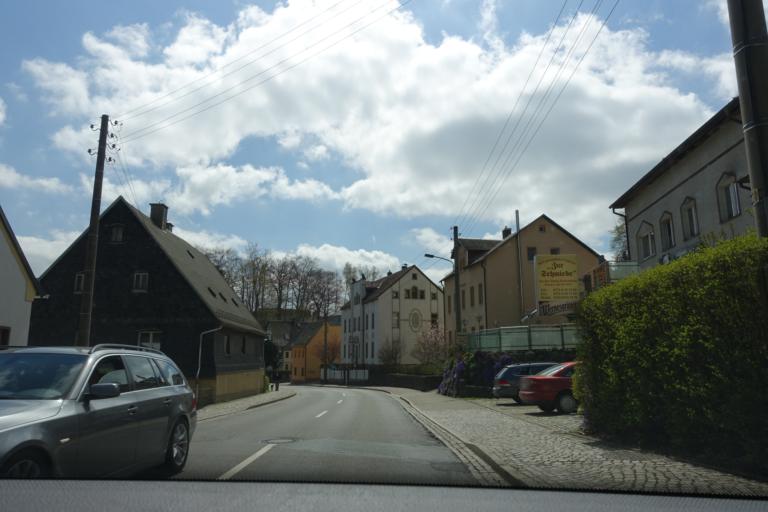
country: DE
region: Saxony
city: Limbach-Oberfrohna
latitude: 50.8325
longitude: 12.8188
